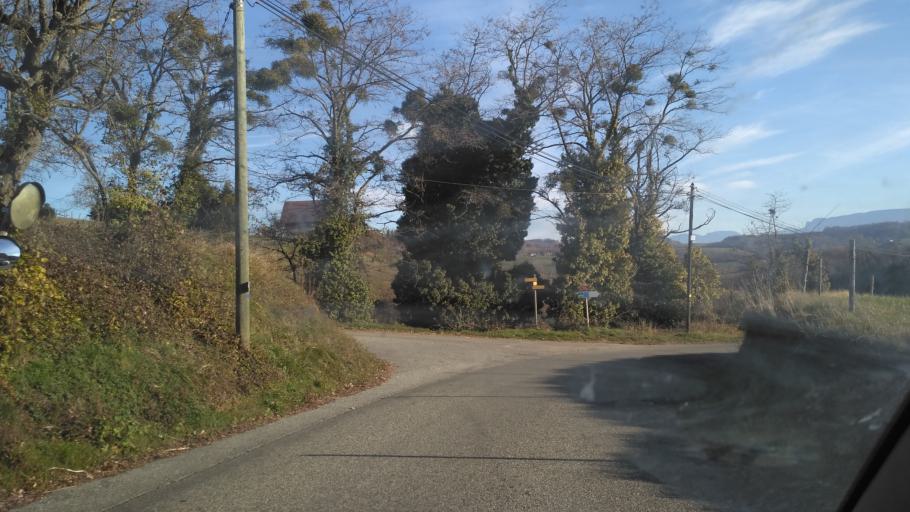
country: FR
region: Rhone-Alpes
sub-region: Departement de l'Isere
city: Saint-Antoine-l'Abbaye
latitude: 45.1776
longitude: 5.2059
